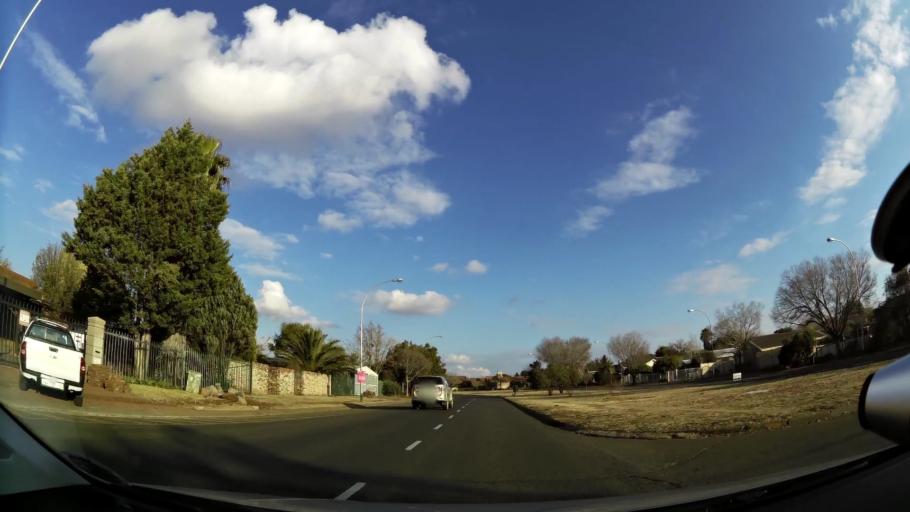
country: ZA
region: Orange Free State
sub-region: Mangaung Metropolitan Municipality
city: Bloemfontein
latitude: -29.1513
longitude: 26.1798
